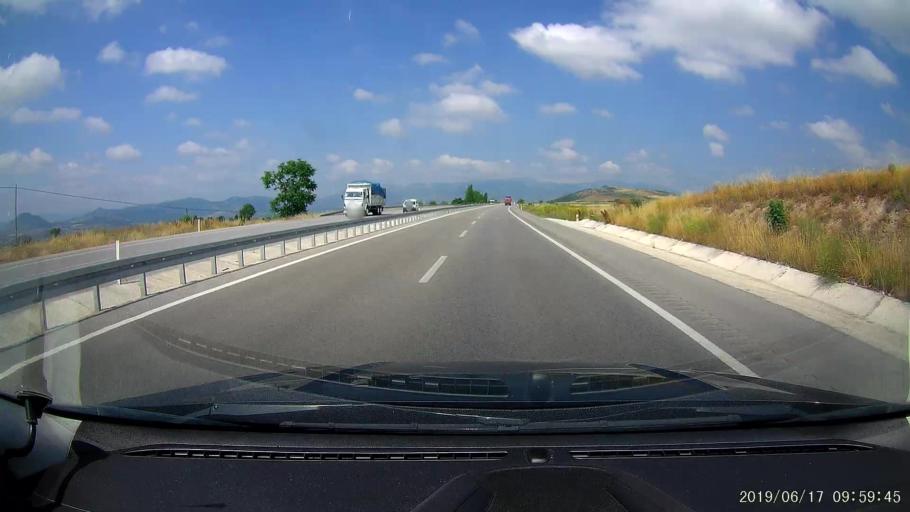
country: TR
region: Amasya
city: Alicik
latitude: 40.8664
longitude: 35.3063
